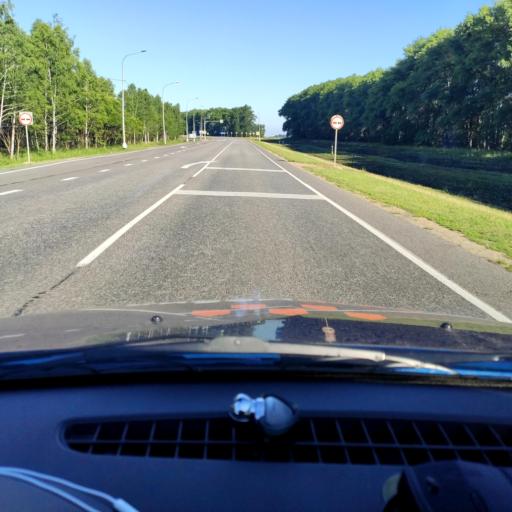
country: RU
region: Orjol
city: Pokrovskoye
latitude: 52.6404
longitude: 36.6743
